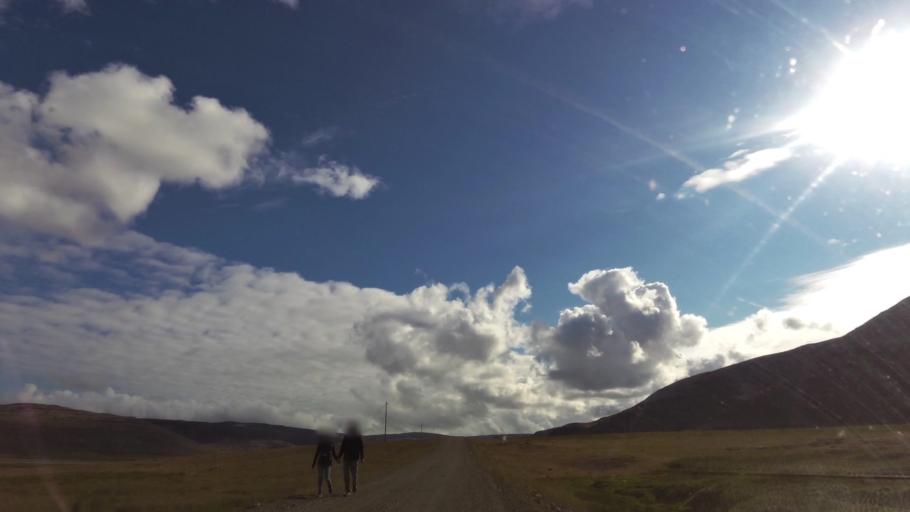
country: IS
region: West
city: Olafsvik
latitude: 65.5886
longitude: -24.1263
